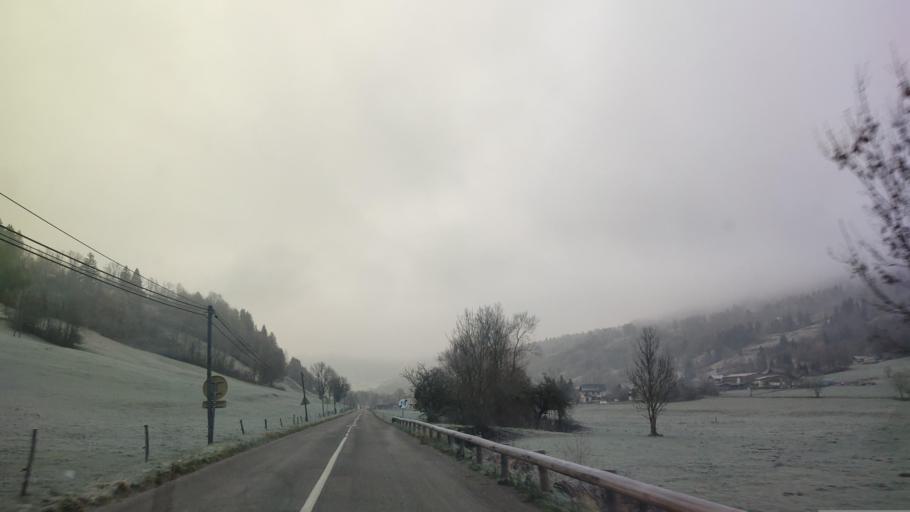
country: FR
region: Rhone-Alpes
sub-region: Departement de la Savoie
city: Coise-Saint-Jean-Pied-Gauthier
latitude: 45.6282
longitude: 6.1537
